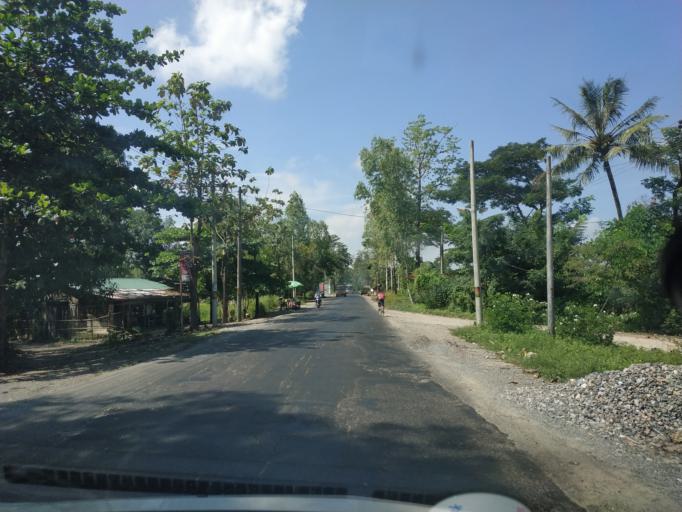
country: MM
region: Ayeyarwady
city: Nyaungdon
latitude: 17.0462
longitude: 95.5478
